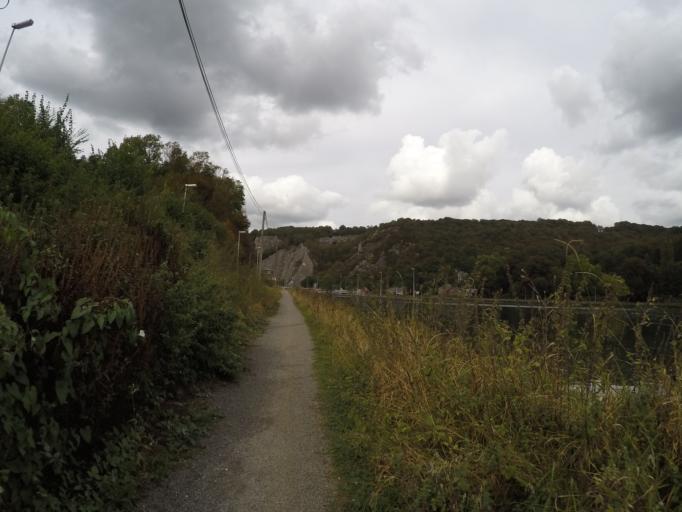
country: BE
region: Wallonia
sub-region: Province de Namur
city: Yvoir
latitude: 50.3325
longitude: 4.8717
